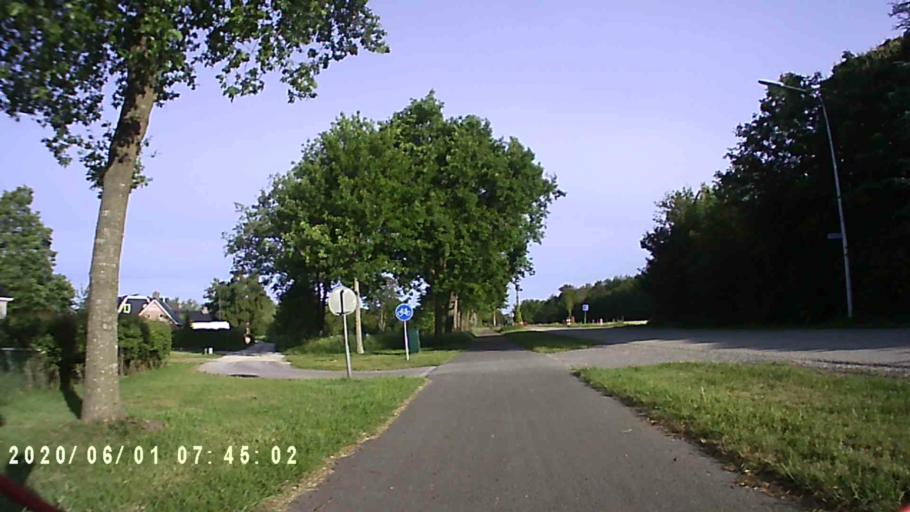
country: NL
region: Friesland
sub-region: Gemeente Dantumadiel
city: Rinsumageast
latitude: 53.2923
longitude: 5.9645
